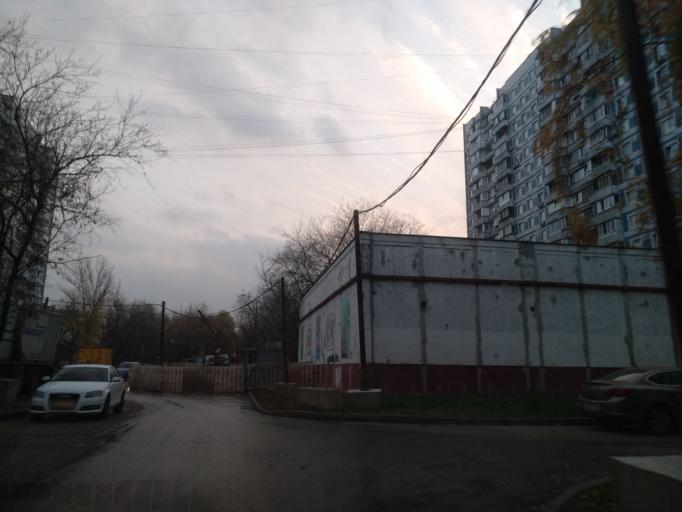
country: RU
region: Moscow
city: Leonovo
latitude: 55.8661
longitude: 37.6560
